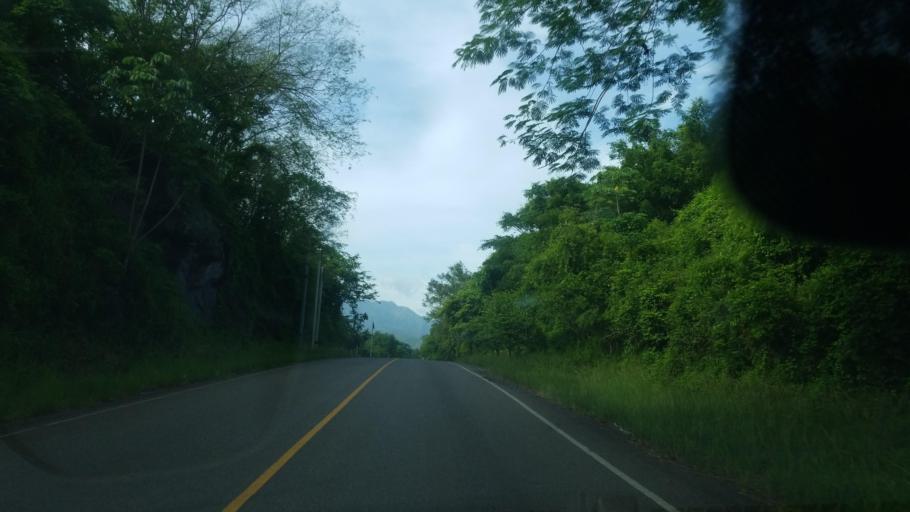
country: HN
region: Santa Barbara
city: Trinidad
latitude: 15.1314
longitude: -88.2507
